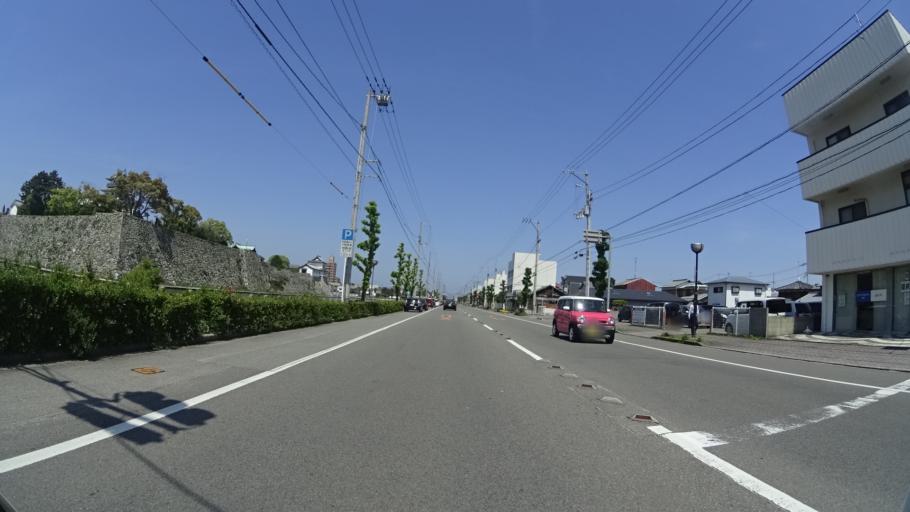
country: JP
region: Ehime
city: Saijo
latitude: 34.0616
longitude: 133.0063
